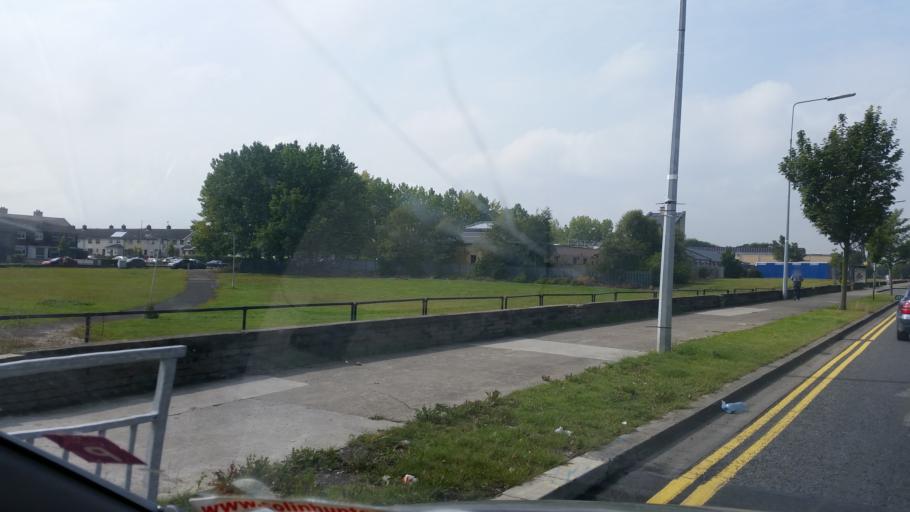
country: IE
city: Bonnybrook
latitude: 53.3952
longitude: -6.2142
